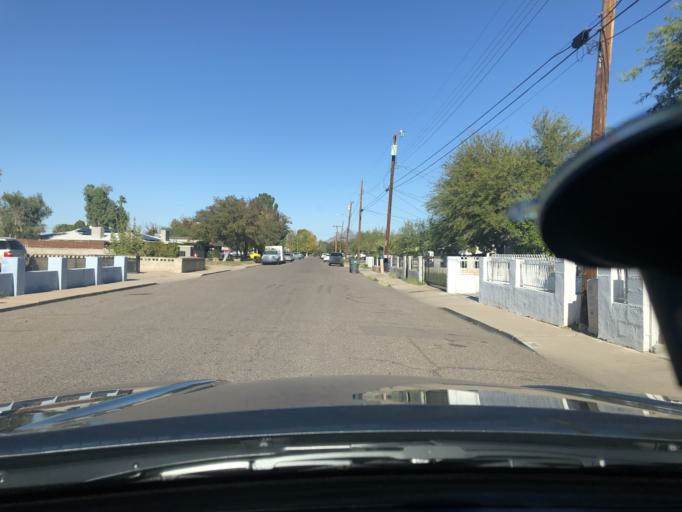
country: US
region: Arizona
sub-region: Maricopa County
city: Phoenix
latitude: 33.4684
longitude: -112.0266
